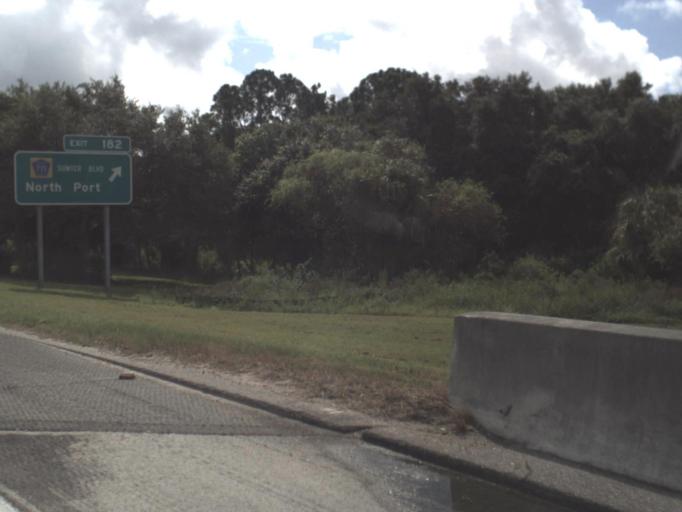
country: US
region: Florida
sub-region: Sarasota County
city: North Port
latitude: 27.0992
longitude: -82.2090
